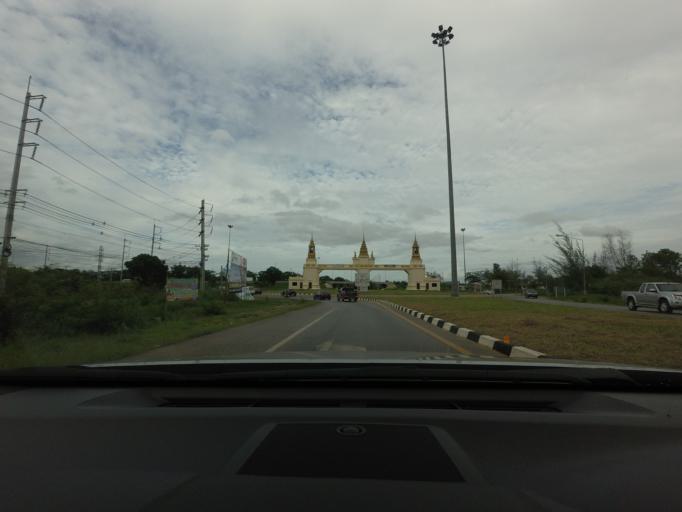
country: TH
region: Prachuap Khiri Khan
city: Hua Hin
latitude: 12.5764
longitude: 99.8650
